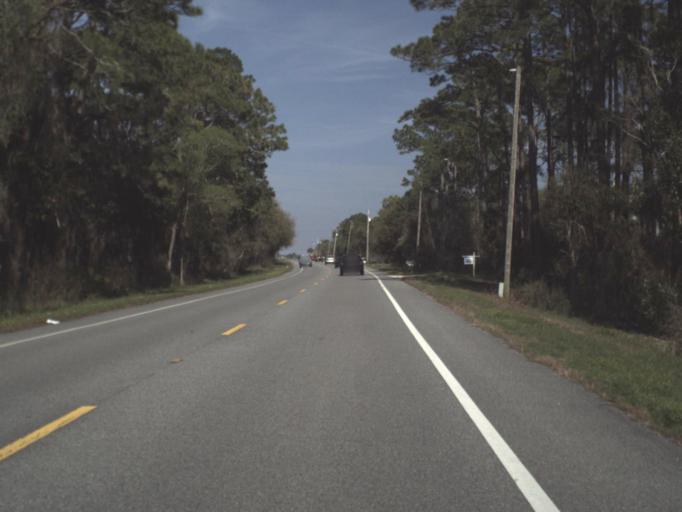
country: US
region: Florida
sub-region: Franklin County
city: Carrabelle
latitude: 29.8098
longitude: -84.7254
